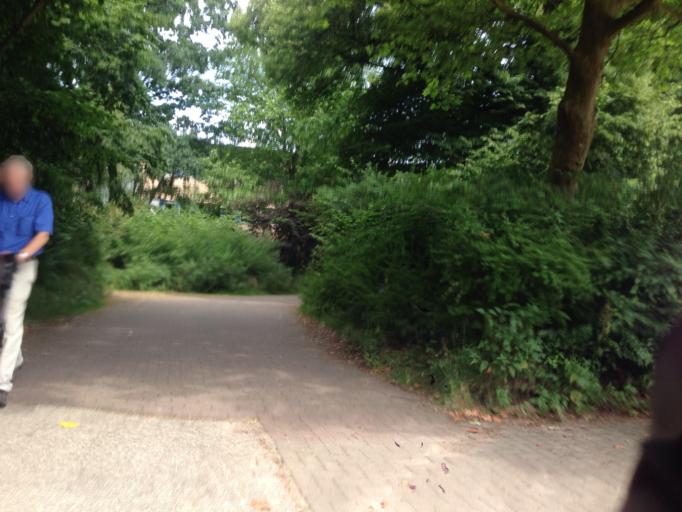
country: DE
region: Hamburg
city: Farmsen-Berne
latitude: 53.5993
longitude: 10.1510
